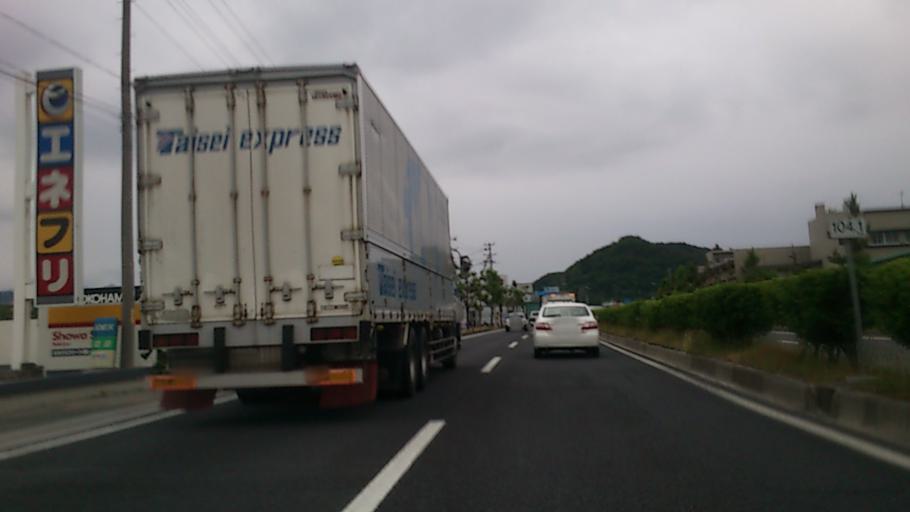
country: JP
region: Yamagata
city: Tendo
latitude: 38.3581
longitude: 140.3888
